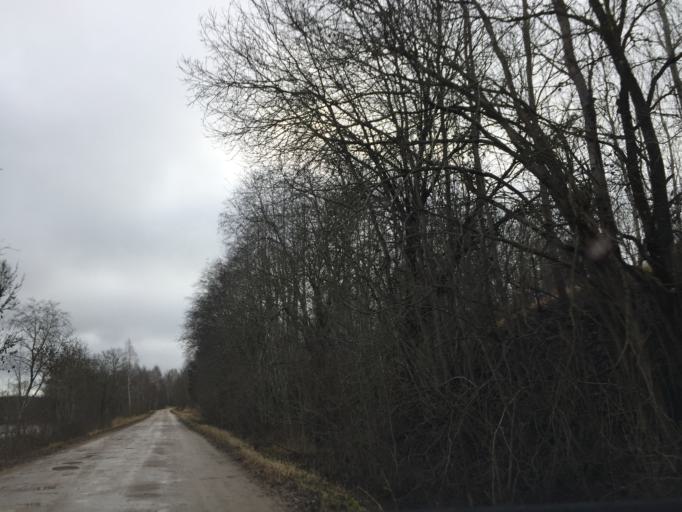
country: LV
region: Broceni
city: Broceni
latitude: 56.6616
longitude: 22.5534
